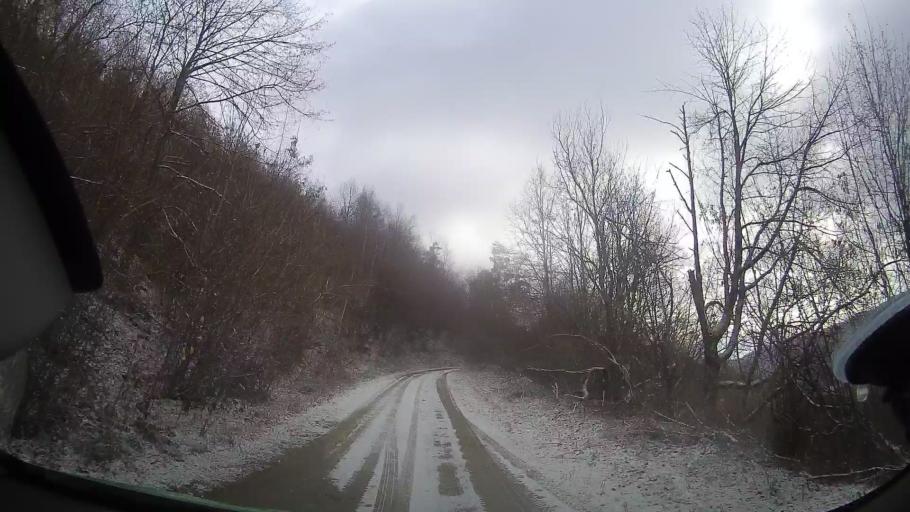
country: RO
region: Cluj
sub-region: Comuna Valea Ierii
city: Valea Ierii
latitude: 46.6520
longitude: 23.3510
